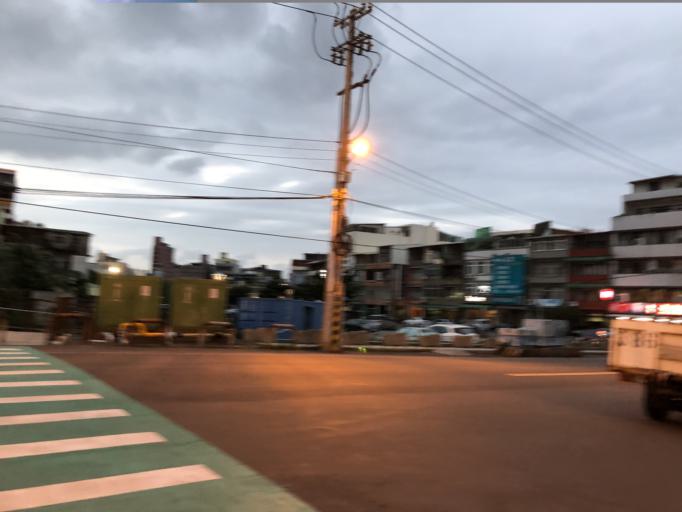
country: TW
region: Taiwan
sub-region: Hsinchu
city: Zhubei
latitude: 24.7332
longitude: 121.0909
